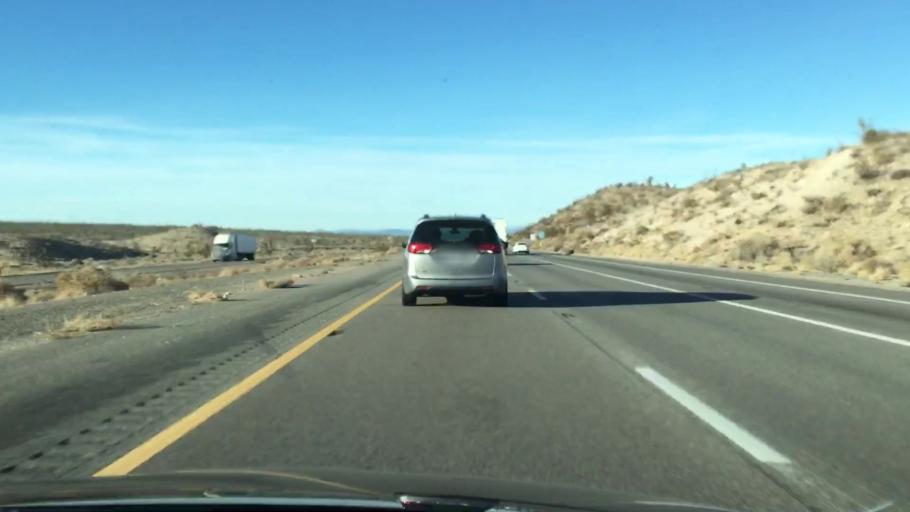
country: US
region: Nevada
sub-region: Clark County
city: Sandy Valley
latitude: 35.4006
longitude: -115.7997
